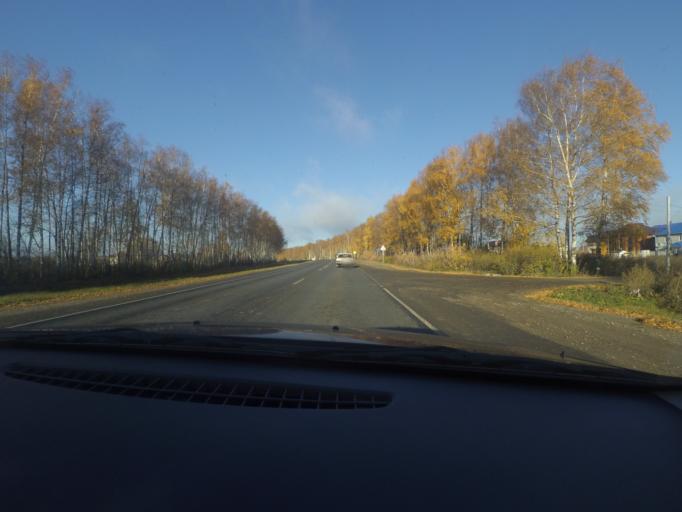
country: RU
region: Nizjnij Novgorod
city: Nizhniy Novgorod
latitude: 56.2140
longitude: 43.9654
